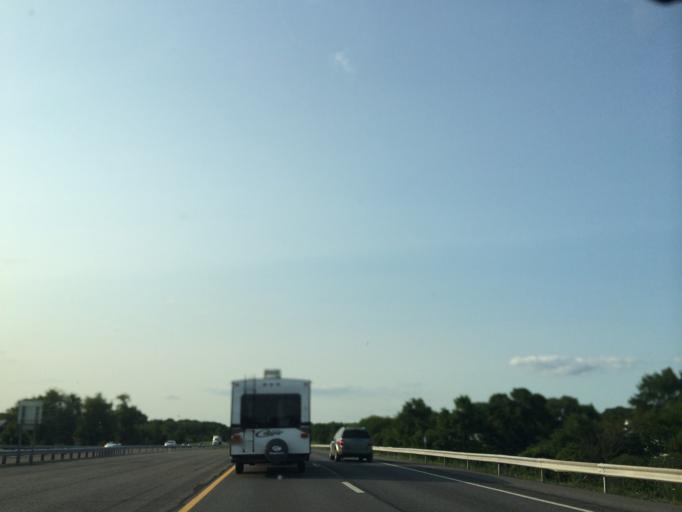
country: US
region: New York
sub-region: Albany County
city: Ravena
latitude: 42.4727
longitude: -73.8060
